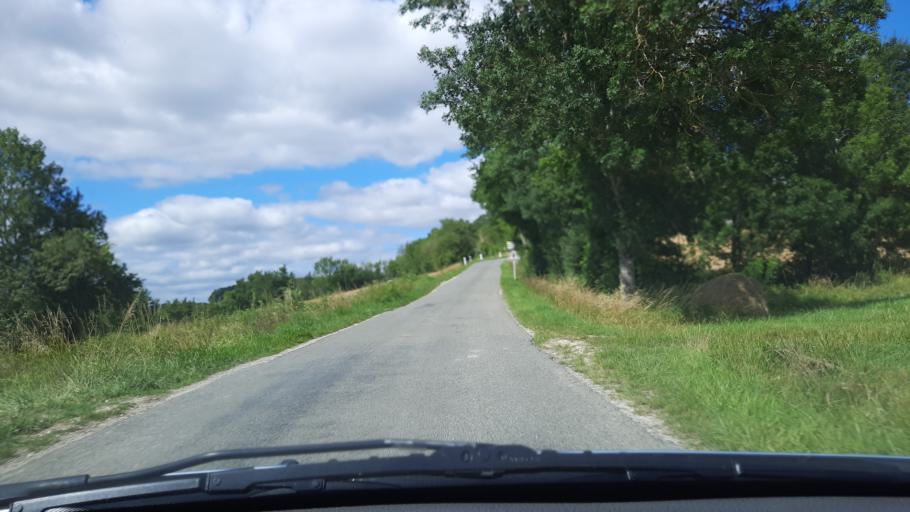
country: FR
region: Midi-Pyrenees
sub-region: Departement du Lot
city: Castelnau-Montratier
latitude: 44.2964
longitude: 1.4441
